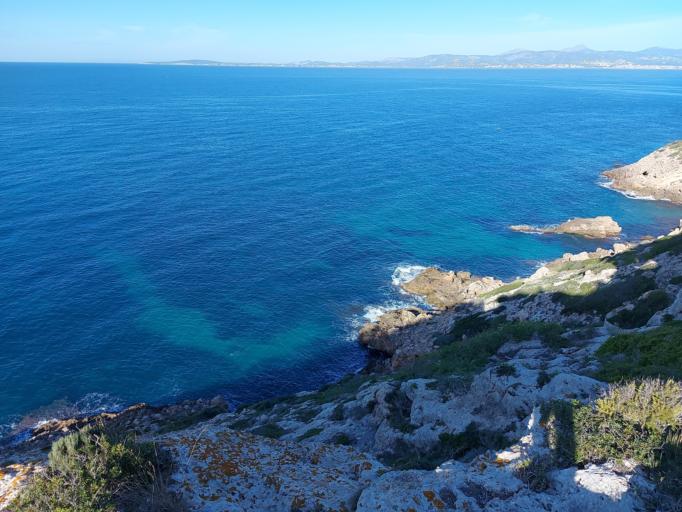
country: ES
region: Balearic Islands
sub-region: Illes Balears
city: s'Arenal
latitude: 39.4659
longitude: 2.7300
